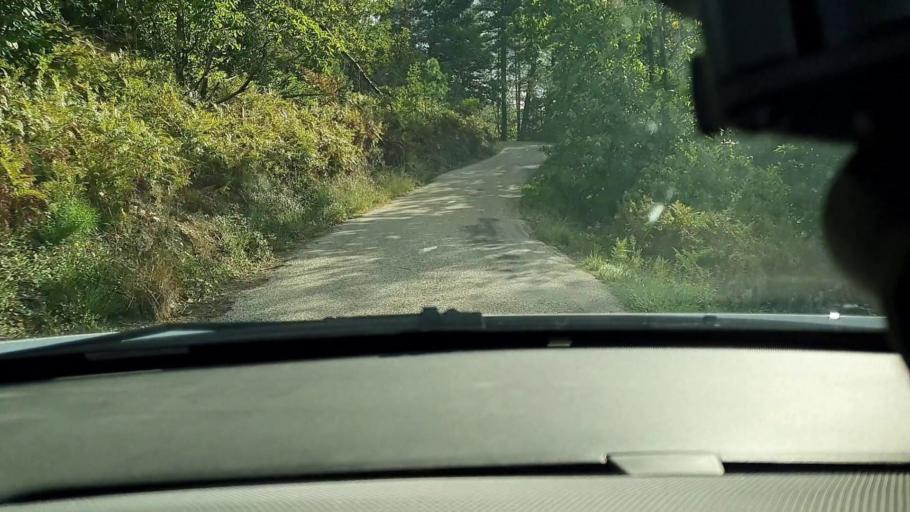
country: FR
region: Languedoc-Roussillon
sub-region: Departement du Gard
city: Besseges
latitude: 44.3491
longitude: 4.0070
